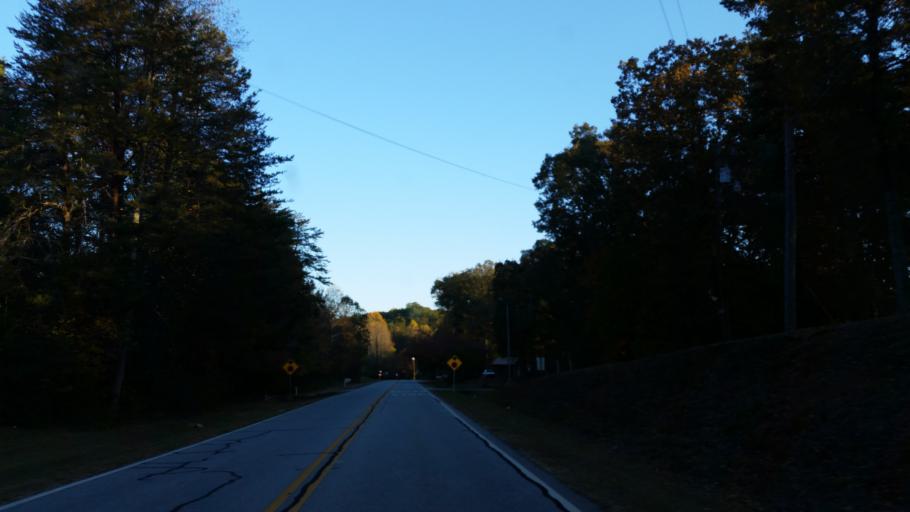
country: US
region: Georgia
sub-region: Lumpkin County
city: Dahlonega
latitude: 34.5222
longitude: -84.0484
